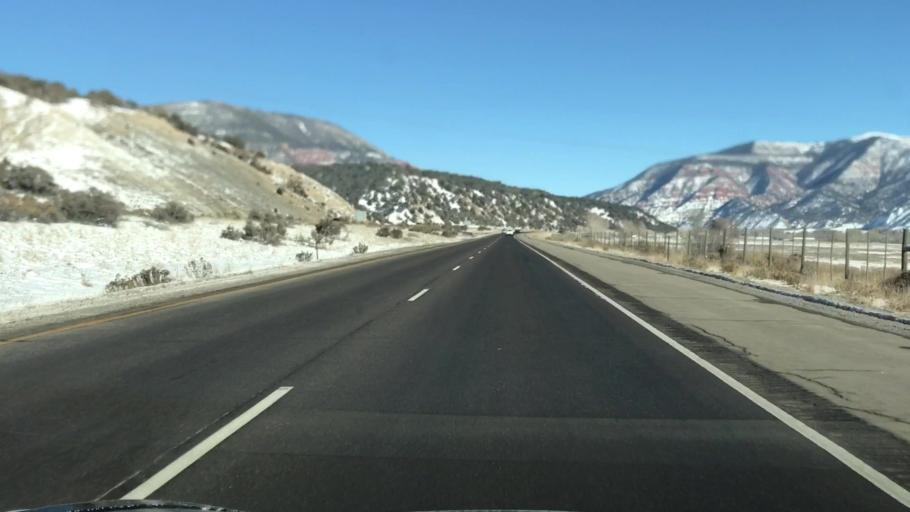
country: US
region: Colorado
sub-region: Eagle County
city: Eagle
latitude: 39.6698
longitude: -106.8053
